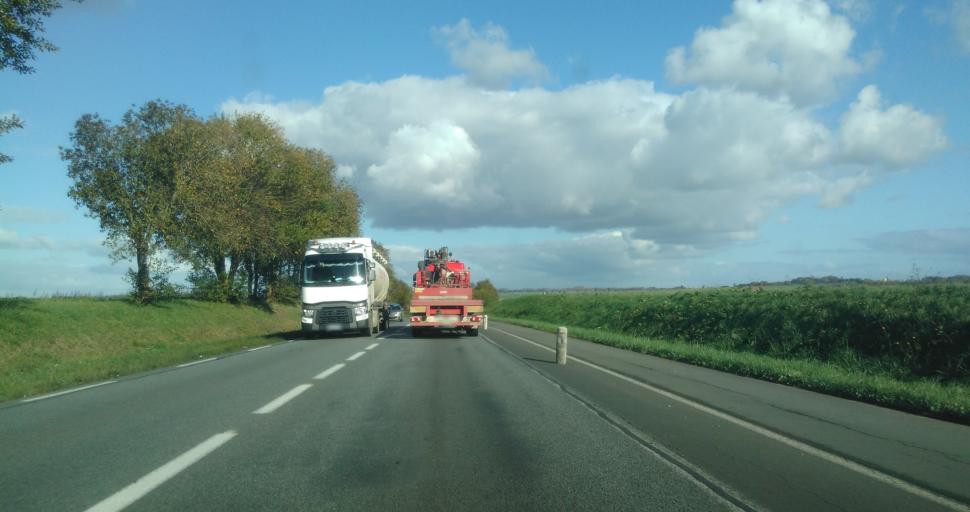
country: FR
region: Nord-Pas-de-Calais
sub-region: Departement du Pas-de-Calais
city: Maroeuil
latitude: 50.3189
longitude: 2.7261
